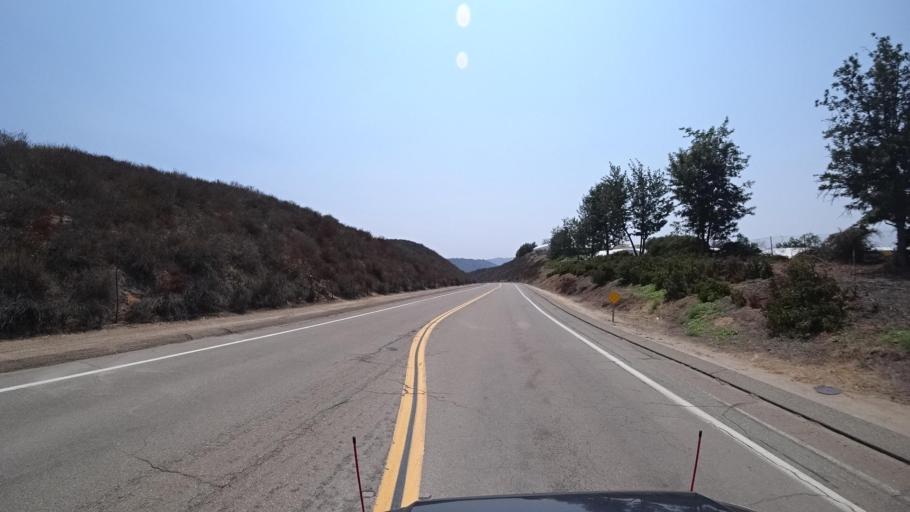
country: US
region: California
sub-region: San Diego County
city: Bonsall
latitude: 33.2919
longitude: -117.1515
